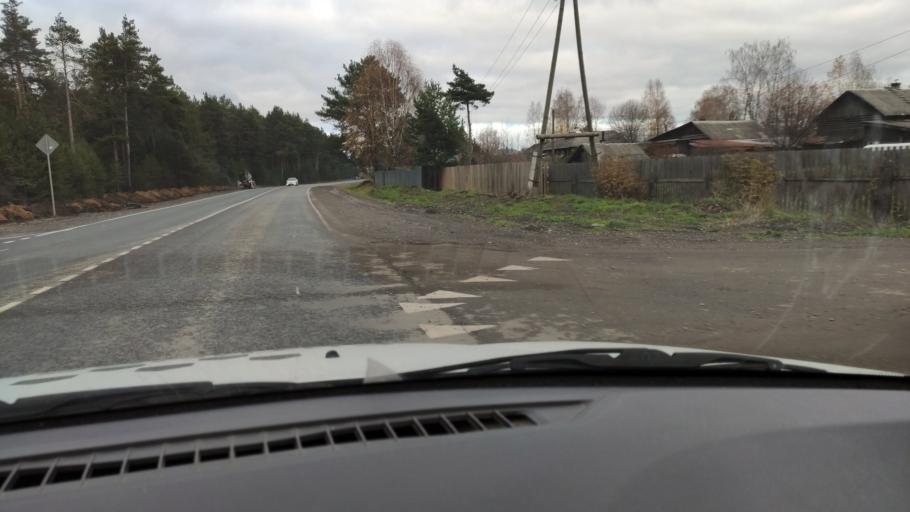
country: RU
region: Kirov
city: Belaya Kholunitsa
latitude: 58.8524
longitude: 50.8320
